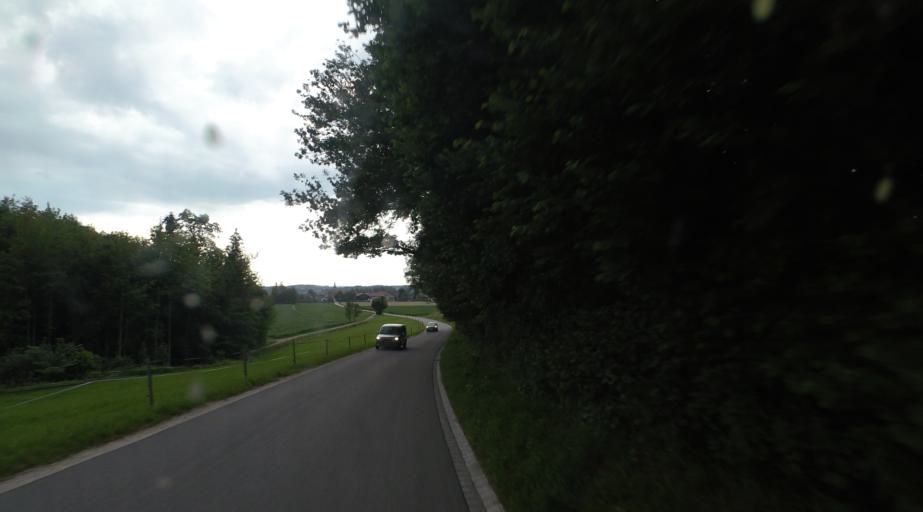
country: DE
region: Bavaria
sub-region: Upper Bavaria
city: Grabenstatt
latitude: 47.8361
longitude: 12.5447
